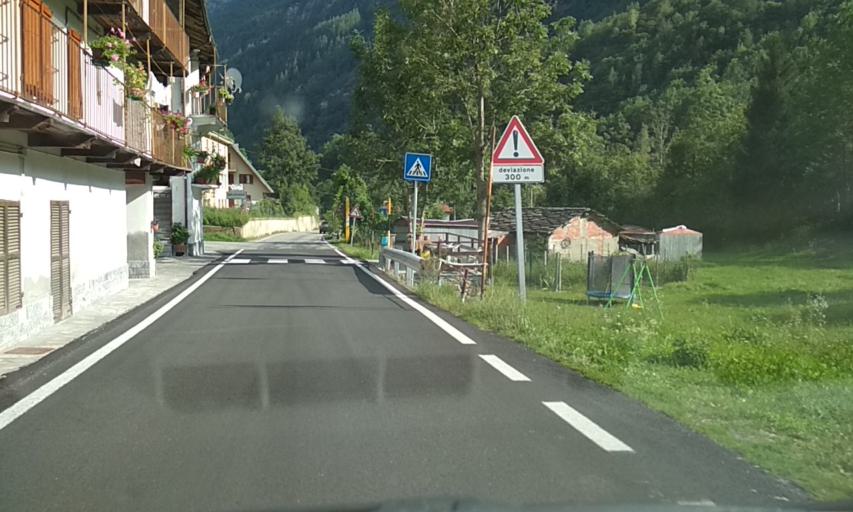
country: IT
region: Piedmont
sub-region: Provincia di Torino
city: Noasca
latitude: 45.4397
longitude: 7.3455
